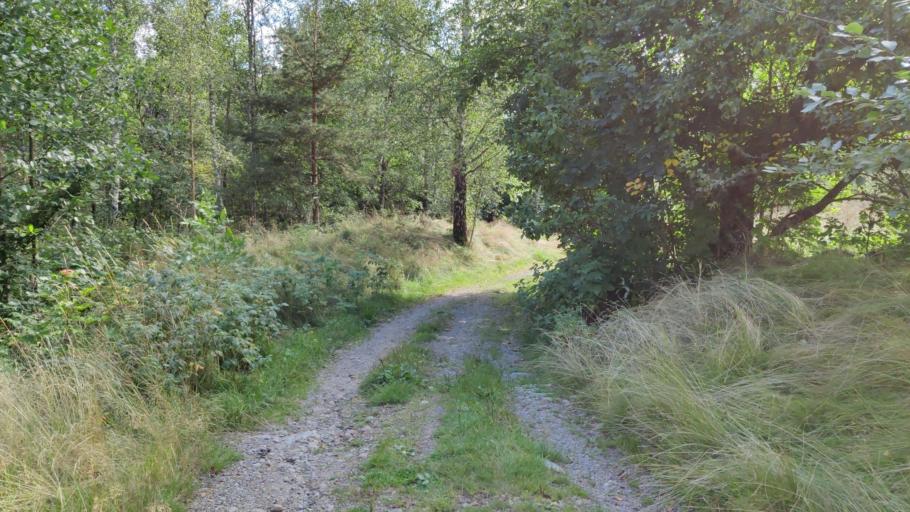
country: SE
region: Vaestra Goetaland
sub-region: Uddevalla Kommun
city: Uddevalla
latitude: 58.3569
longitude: 11.8575
